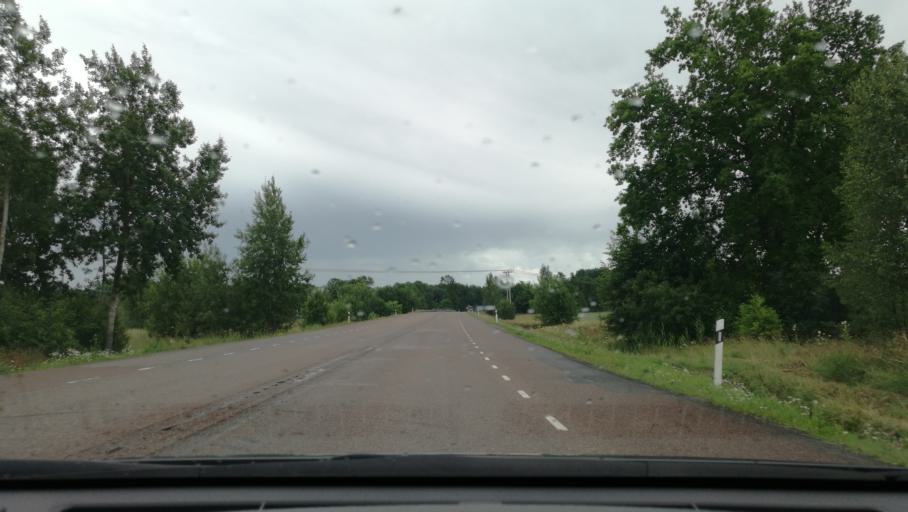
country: SE
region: Vaestmanland
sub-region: Kopings Kommun
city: Koping
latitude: 59.4794
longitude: 15.9882
